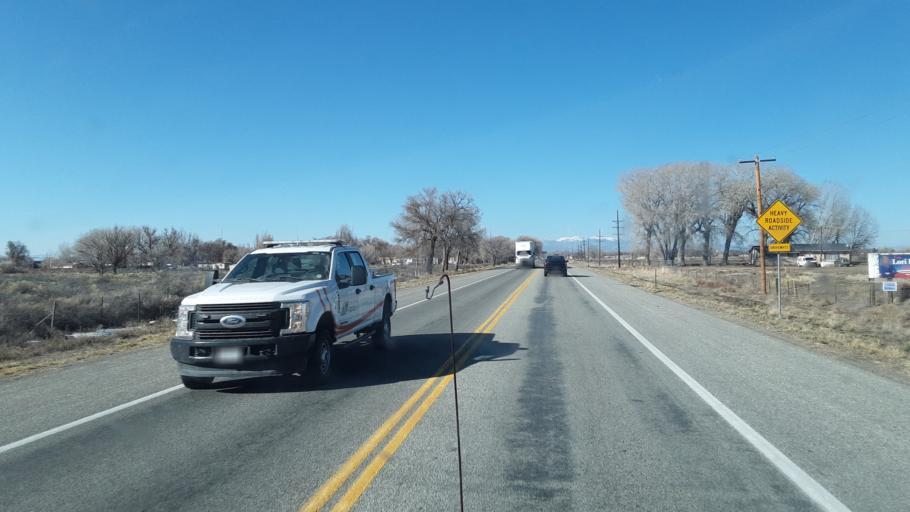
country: US
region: Colorado
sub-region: Alamosa County
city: Alamosa East
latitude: 37.4735
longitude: -105.8265
